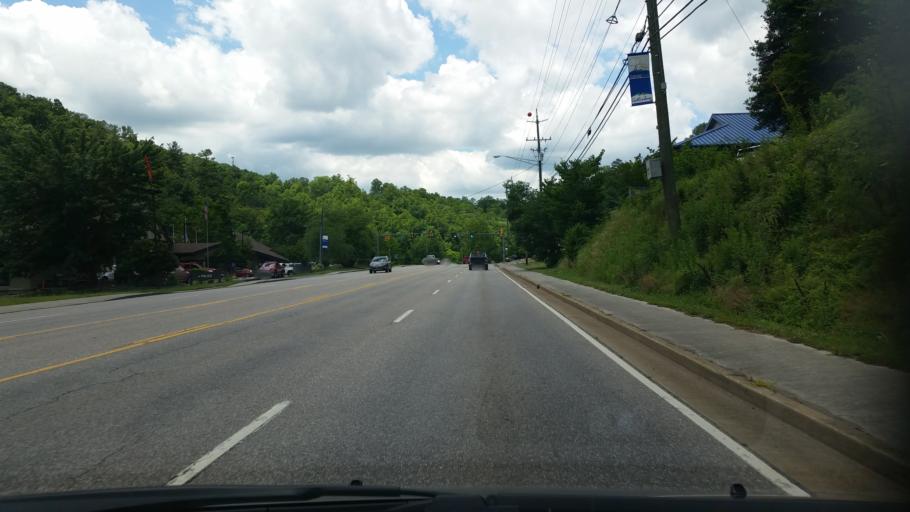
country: US
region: Tennessee
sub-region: Sevier County
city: Gatlinburg
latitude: 35.7264
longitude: -83.4780
